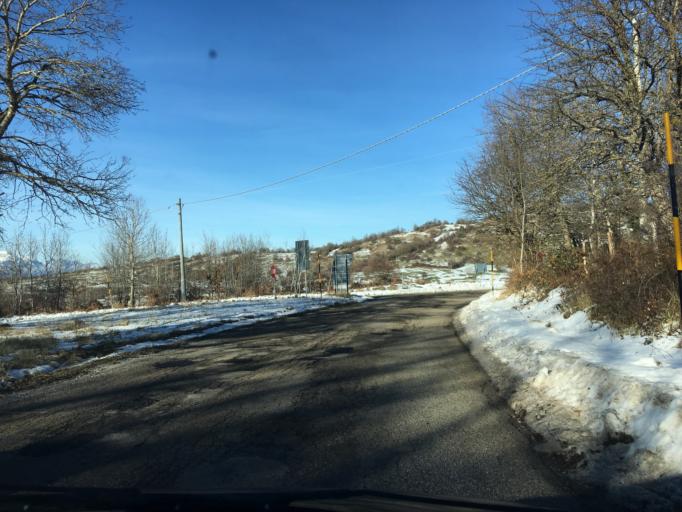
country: IT
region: Abruzzo
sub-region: Provincia di Chieti
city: Rosello
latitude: 41.8631
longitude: 14.3527
